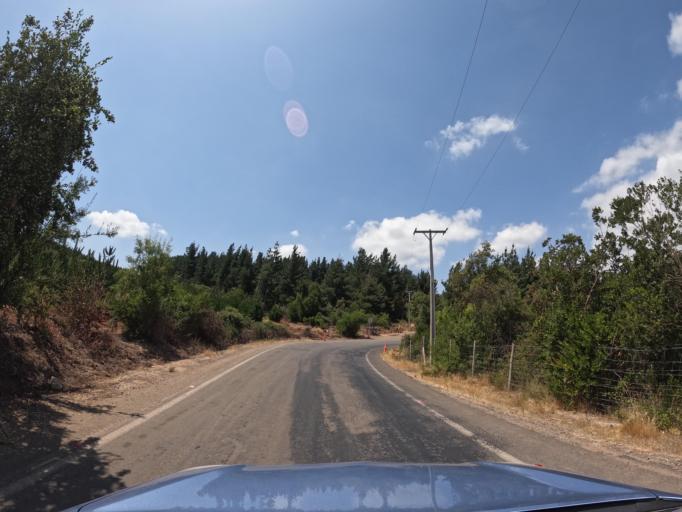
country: CL
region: Maule
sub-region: Provincia de Curico
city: Molina
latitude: -35.1767
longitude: -71.1045
